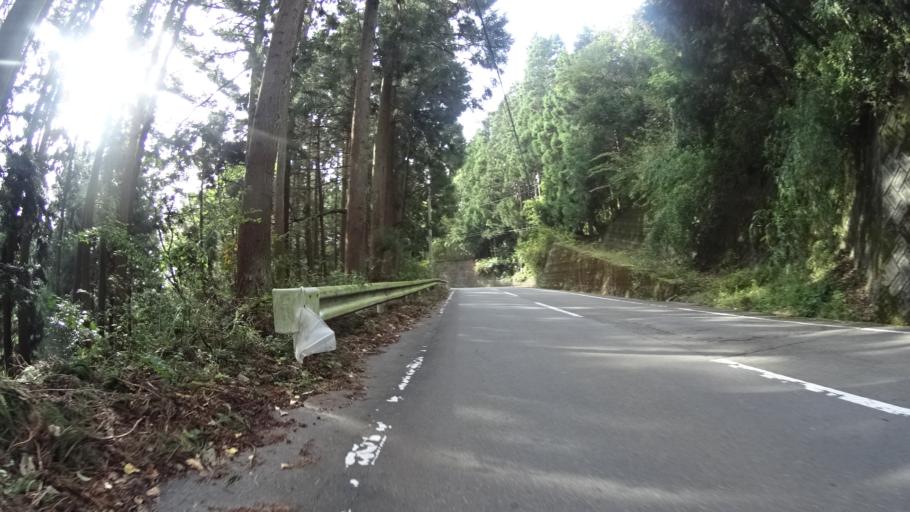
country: JP
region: Yamanashi
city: Uenohara
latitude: 35.6263
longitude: 139.0289
